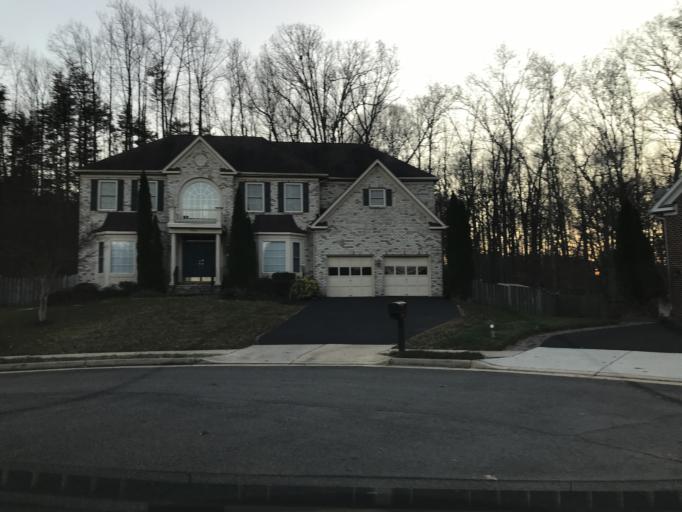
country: US
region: Virginia
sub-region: Fairfax County
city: Franconia
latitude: 38.7891
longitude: -77.1580
